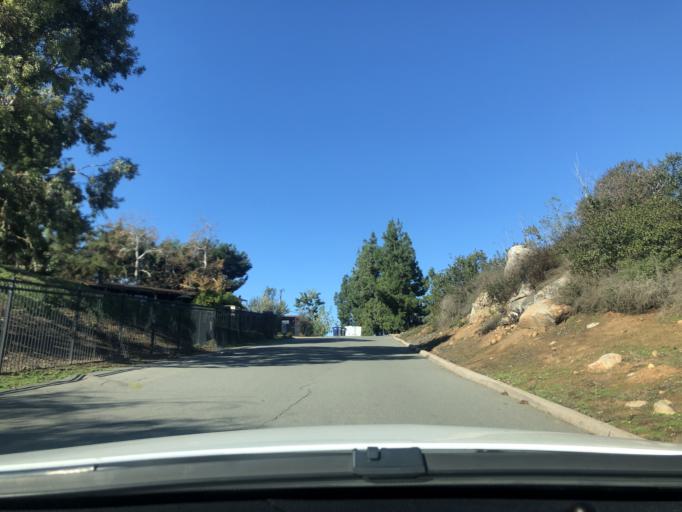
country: US
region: California
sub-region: San Diego County
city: Casa de Oro-Mount Helix
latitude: 32.7734
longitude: -116.9496
